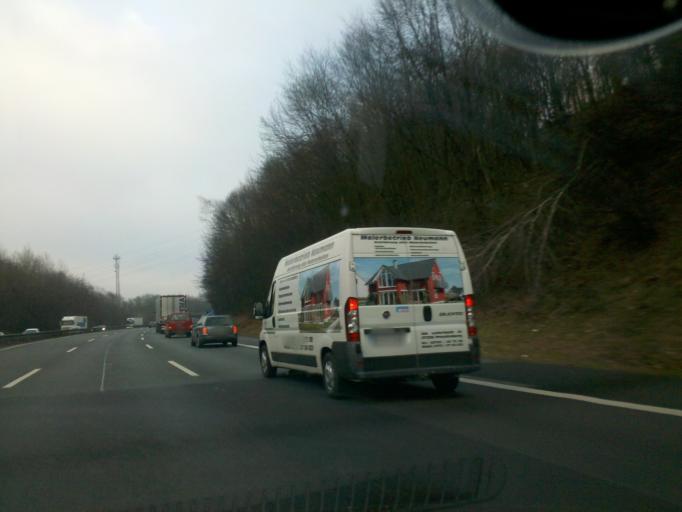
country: DE
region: North Rhine-Westphalia
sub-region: Regierungsbezirk Arnsberg
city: Wilnsdorf
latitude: 50.8185
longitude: 8.0859
